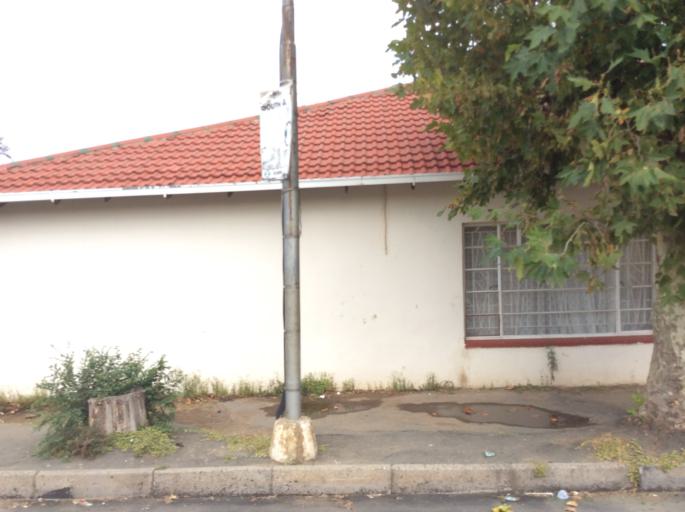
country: LS
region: Mafeteng
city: Mafeteng
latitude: -29.7274
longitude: 27.0372
